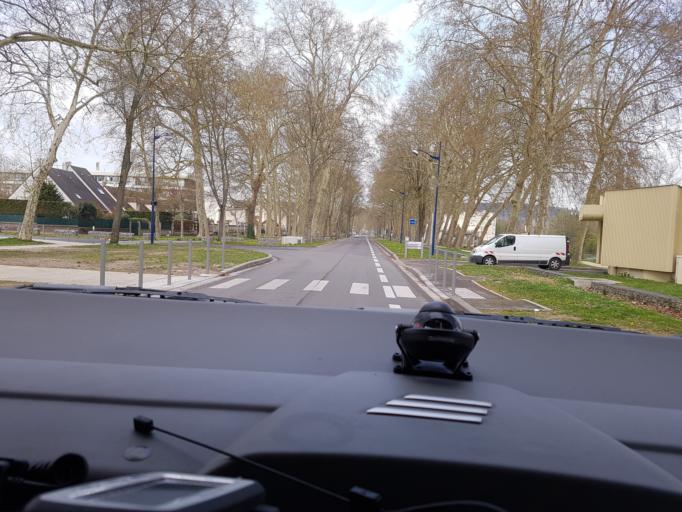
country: FR
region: Picardie
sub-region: Departement de l'Aisne
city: Soissons
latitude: 49.3875
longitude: 3.3288
